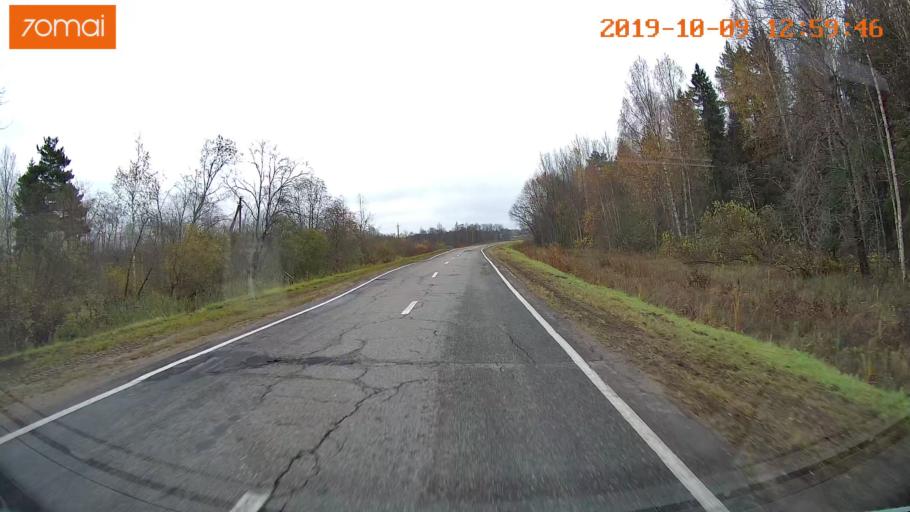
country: RU
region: Jaroslavl
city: Prechistoye
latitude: 58.3821
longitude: 40.4703
